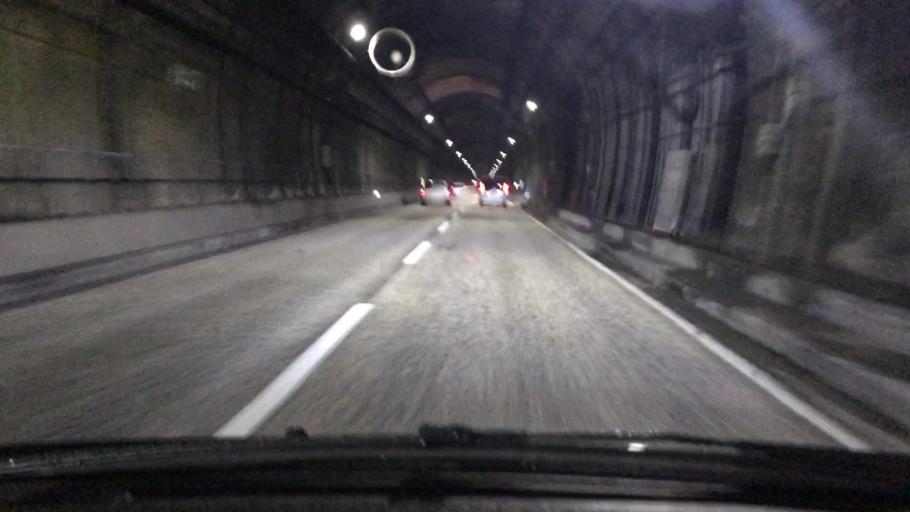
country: JP
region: Hyogo
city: Kobe
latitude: 34.7438
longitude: 135.1704
